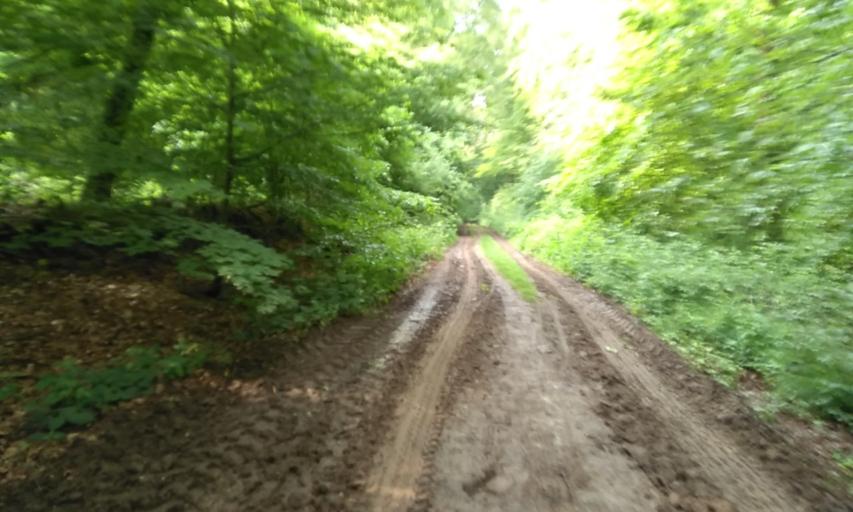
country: DE
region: Lower Saxony
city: Nottensdorf
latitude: 53.4719
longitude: 9.6220
